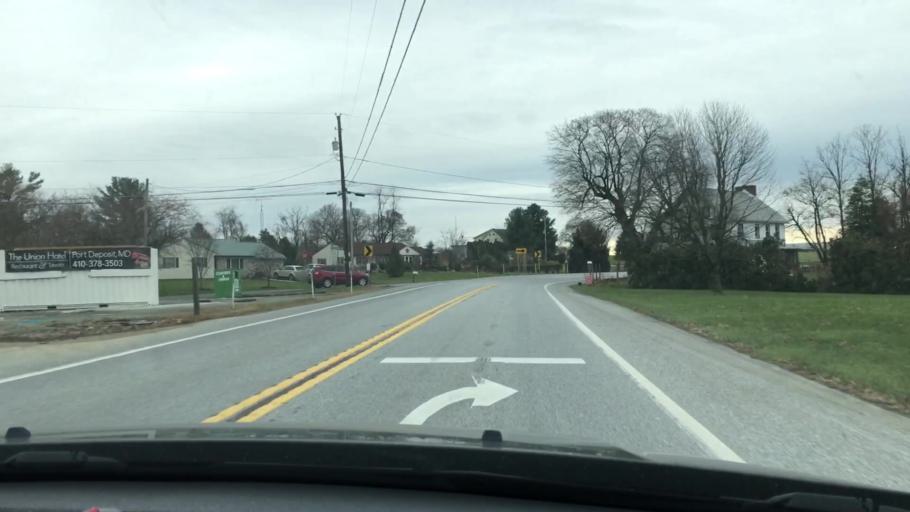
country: US
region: Maryland
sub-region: Cecil County
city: Rising Sun
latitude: 39.7321
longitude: -76.1534
